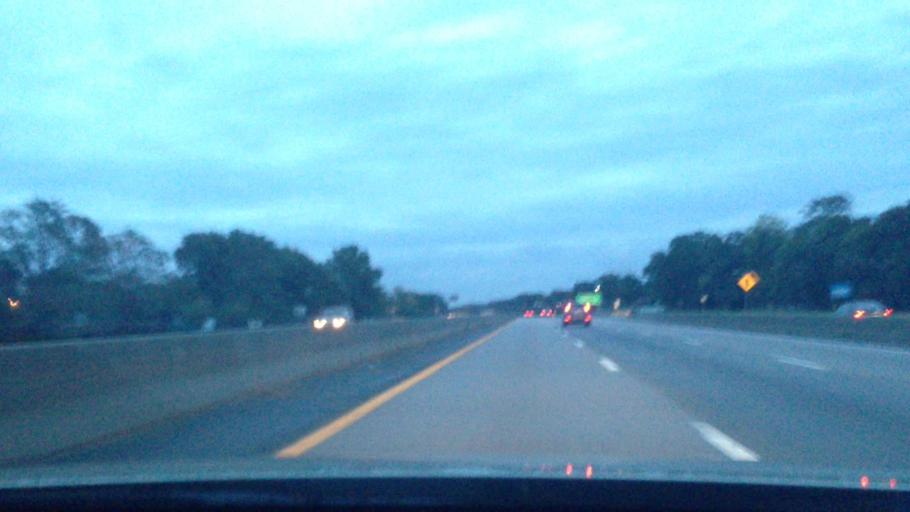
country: US
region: New York
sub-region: Suffolk County
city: Islip Terrace
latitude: 40.7427
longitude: -73.1988
